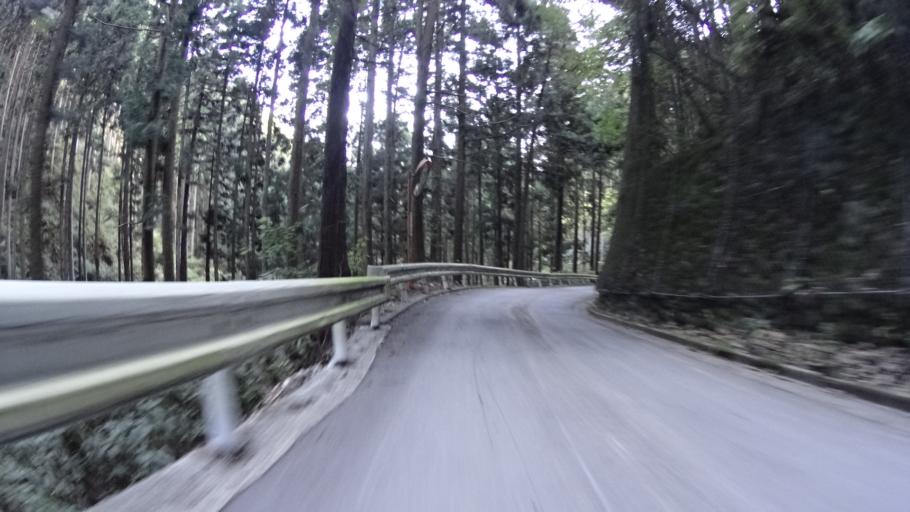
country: JP
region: Yamanashi
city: Uenohara
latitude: 35.6602
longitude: 139.1710
